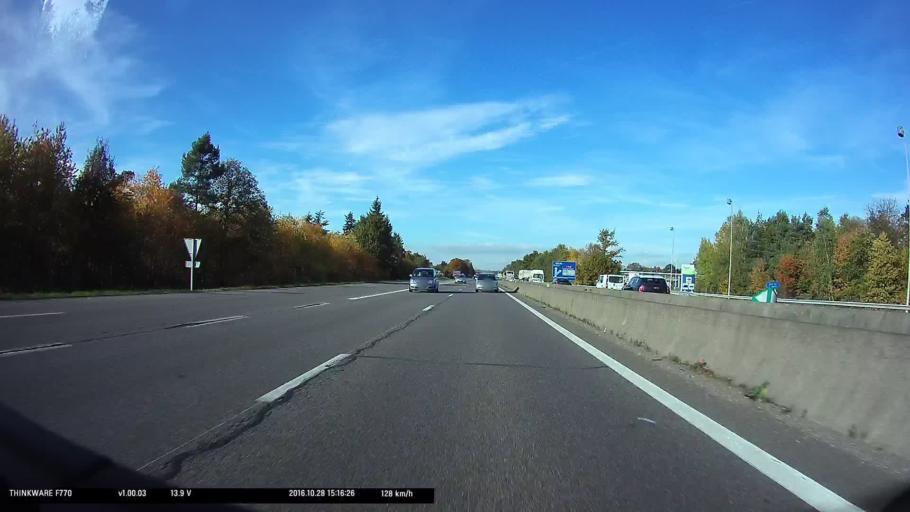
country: FR
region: Alsace
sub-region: Departement du Bas-Rhin
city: Brumath
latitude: 48.7187
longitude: 7.6959
